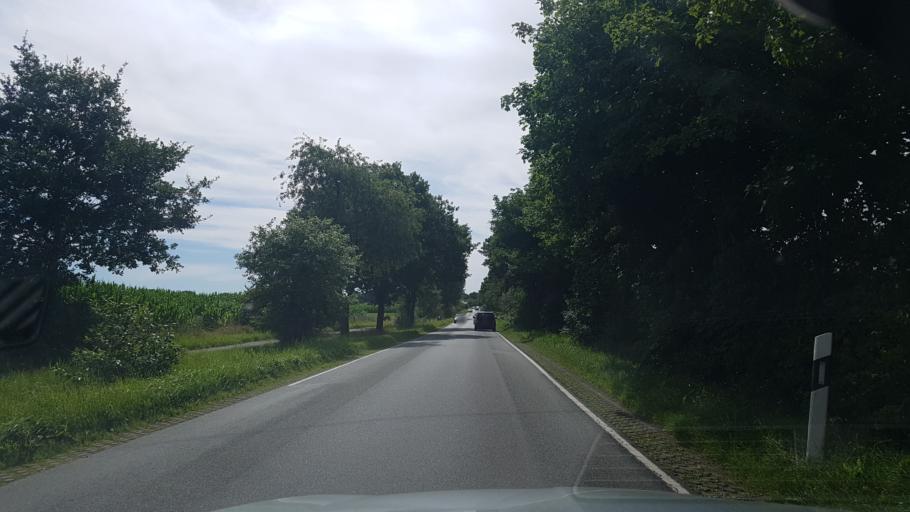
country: DE
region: Schleswig-Holstein
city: Handewitt
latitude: 54.7876
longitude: 9.3213
